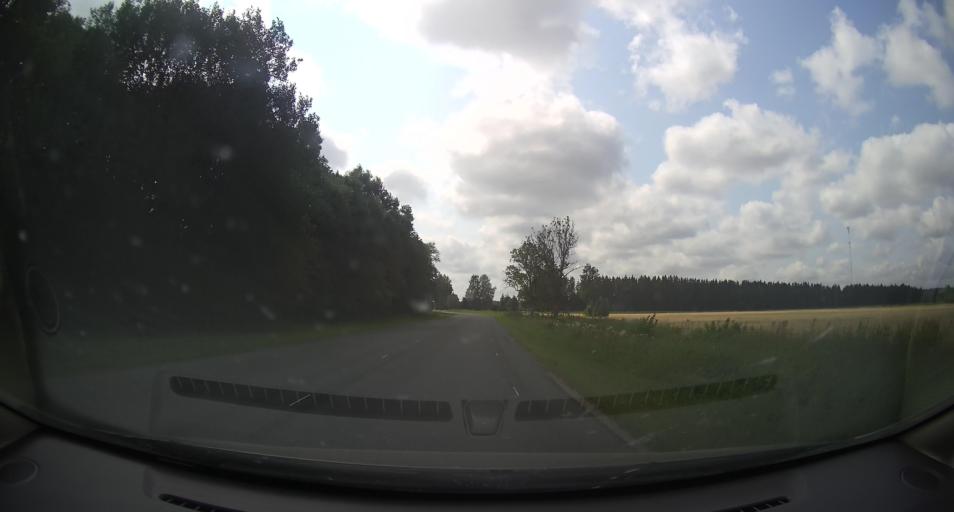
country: EE
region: Paernumaa
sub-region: Audru vald
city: Audru
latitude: 58.4984
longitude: 24.3387
